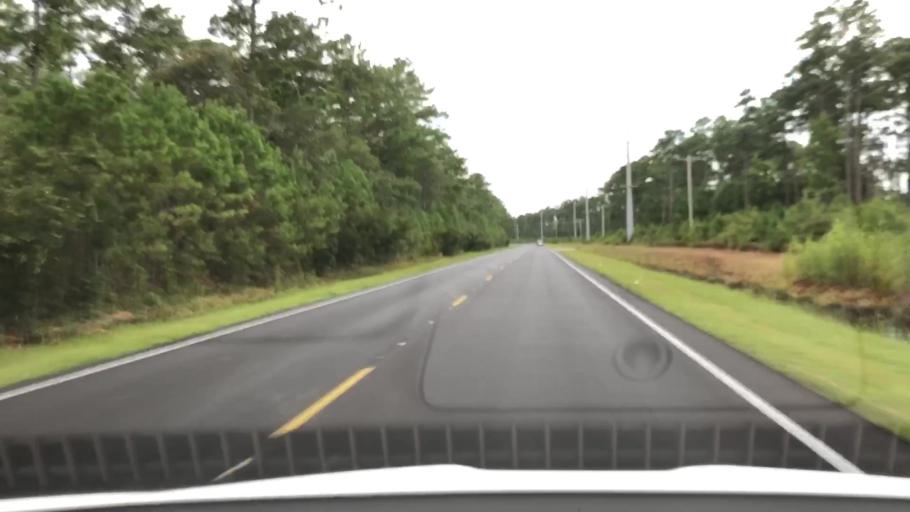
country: US
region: North Carolina
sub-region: Onslow County
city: Swansboro
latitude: 34.7837
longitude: -77.1140
